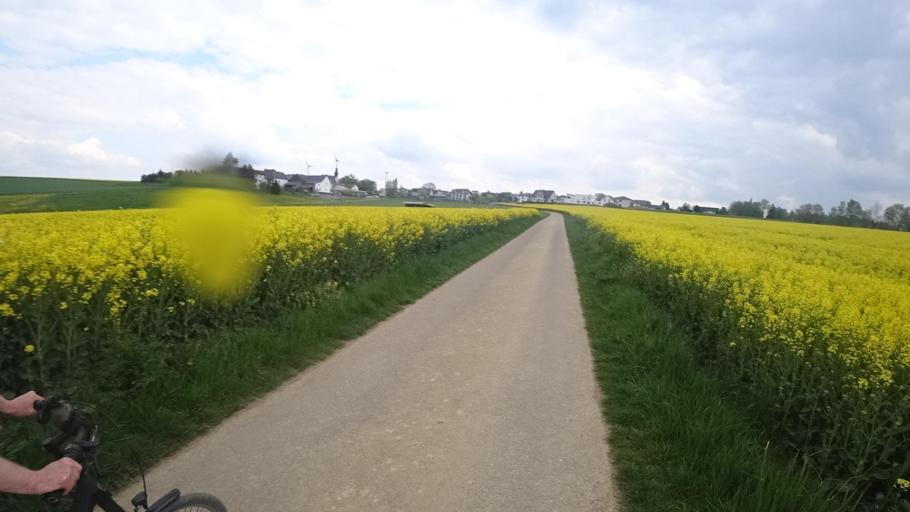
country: DE
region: Rheinland-Pfalz
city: Mutterschied
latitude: 49.9978
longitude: 7.5620
